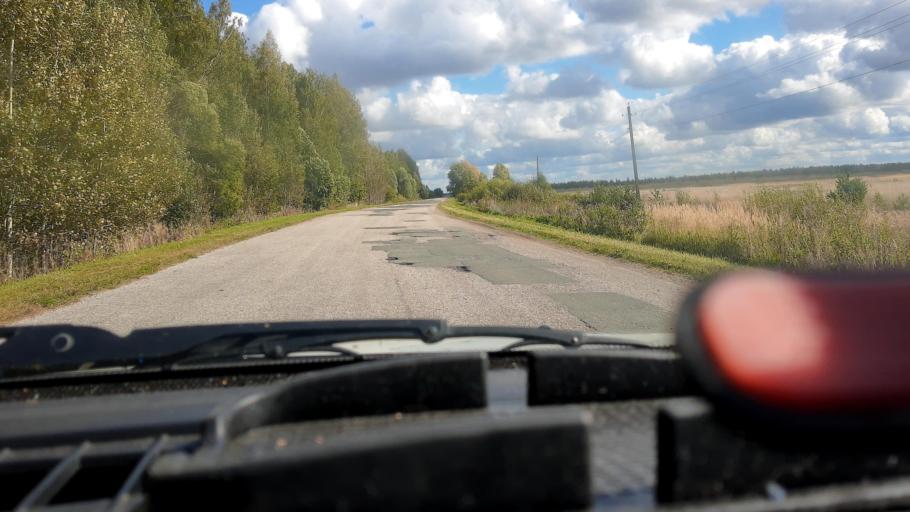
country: RU
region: Mariy-El
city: Kilemary
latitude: 56.9416
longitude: 46.6631
